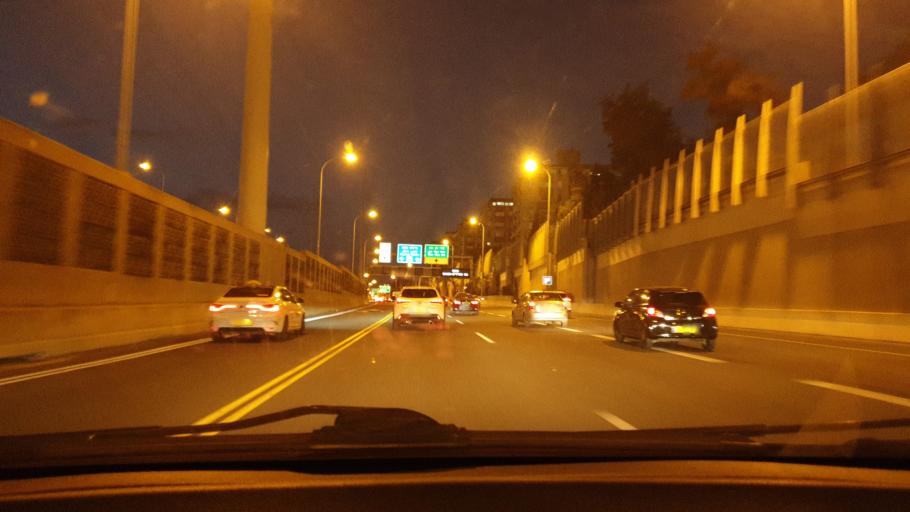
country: IL
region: Tel Aviv
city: Bat Yam
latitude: 32.0179
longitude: 34.7621
